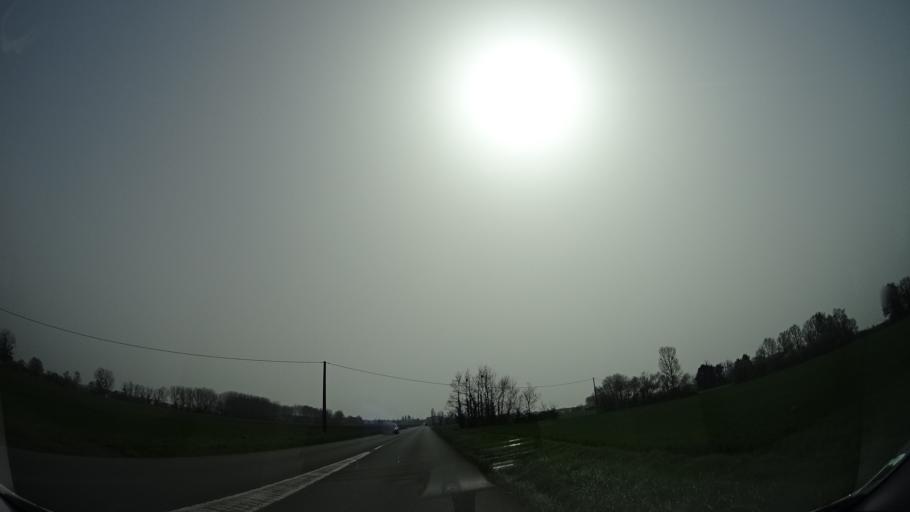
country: FR
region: Pays de la Loire
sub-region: Departement de Maine-et-Loire
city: Doue-la-Fontaine
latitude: 47.2077
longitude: -0.2957
